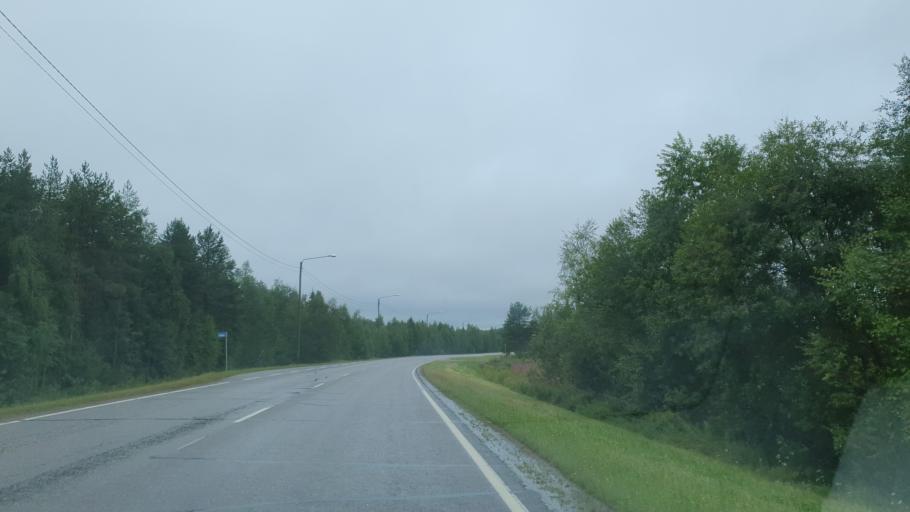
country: FI
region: Lapland
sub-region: Itae-Lappi
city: Kemijaervi
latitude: 66.6943
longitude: 27.5775
